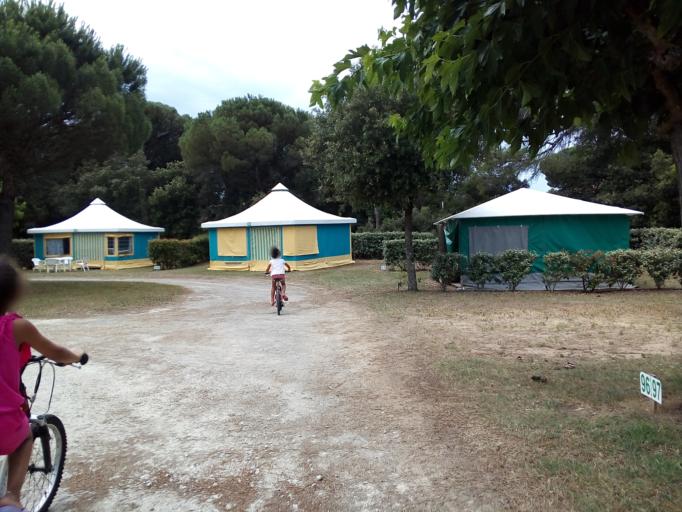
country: FR
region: Poitou-Charentes
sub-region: Departement de la Charente-Maritime
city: Boyard-Ville
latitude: 45.9505
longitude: -1.2495
